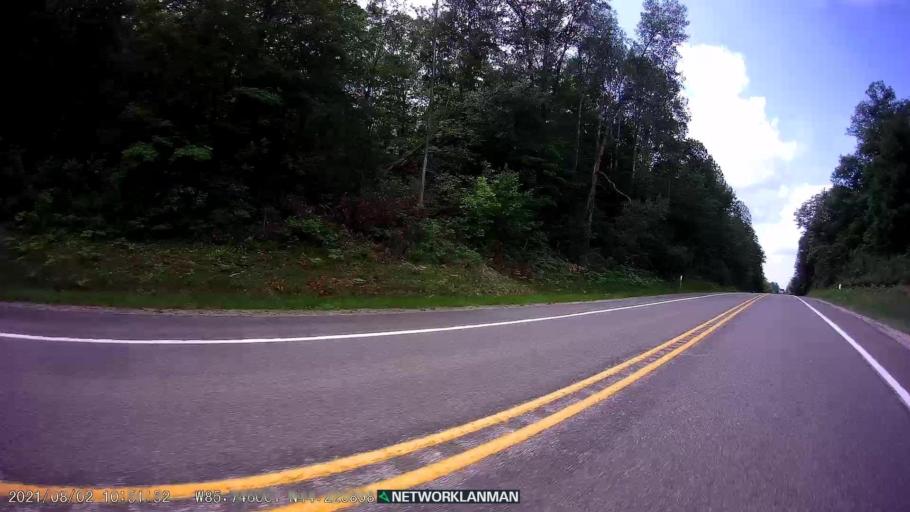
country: US
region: Michigan
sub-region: Lake County
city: Baldwin
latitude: 44.2209
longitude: -85.7464
